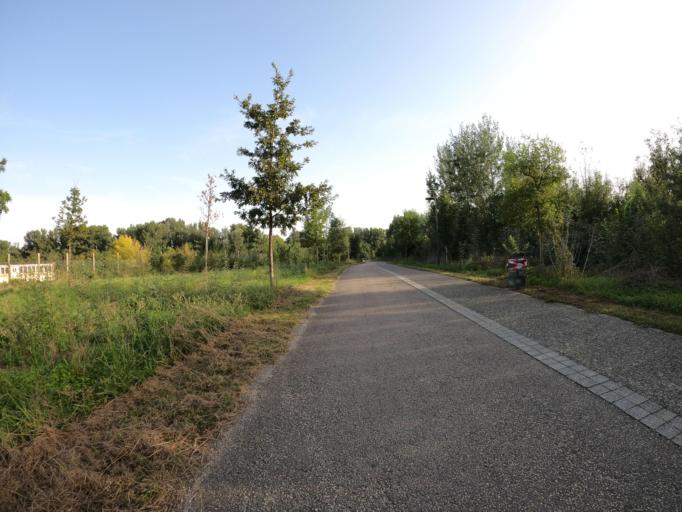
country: FR
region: Midi-Pyrenees
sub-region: Departement de la Haute-Garonne
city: Vieille-Toulouse
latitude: 43.5503
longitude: 1.4300
